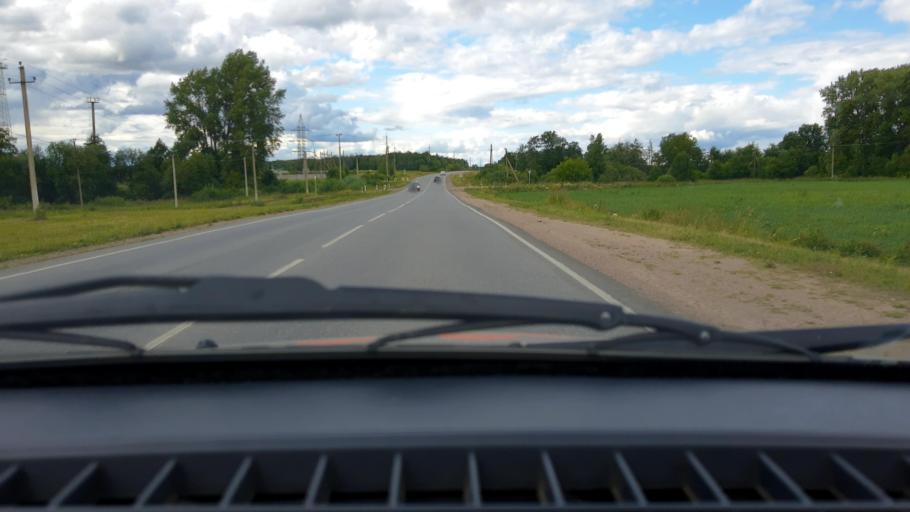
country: RU
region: Bashkortostan
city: Iglino
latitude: 54.8801
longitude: 56.4697
